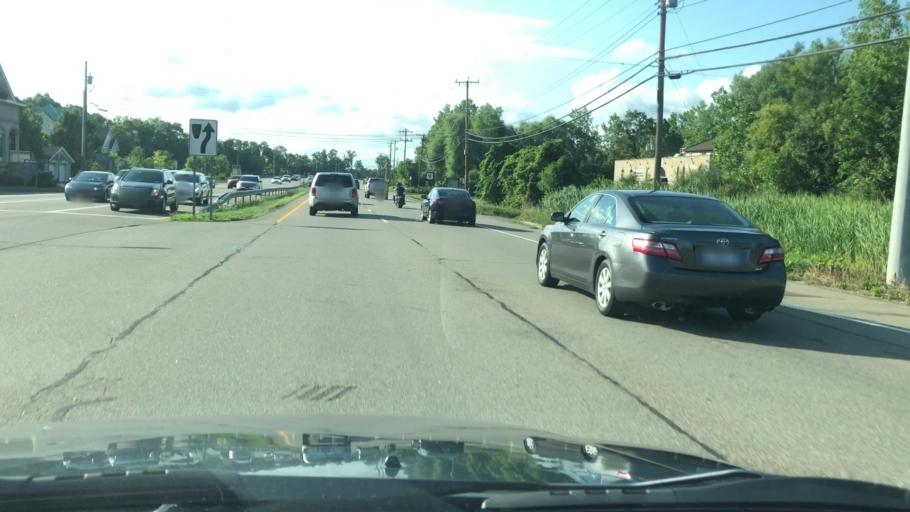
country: US
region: New York
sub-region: Dutchess County
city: Fishkill
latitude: 41.5645
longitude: -73.9054
